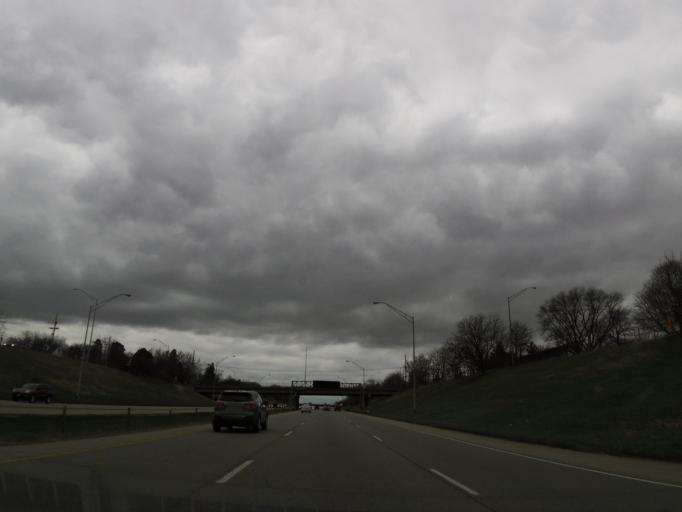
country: US
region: Iowa
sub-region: Linn County
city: Cedar Rapids
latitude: 41.9579
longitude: -91.6710
